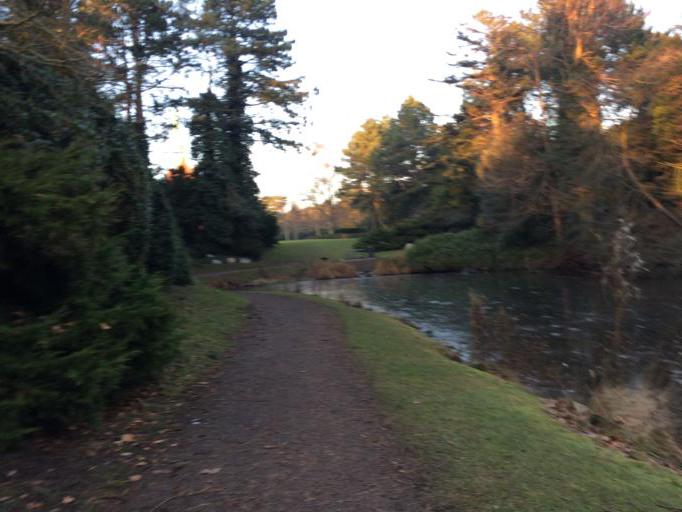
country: DK
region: Capital Region
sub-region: Frederiksberg Kommune
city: Frederiksberg
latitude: 55.6598
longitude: 12.5286
